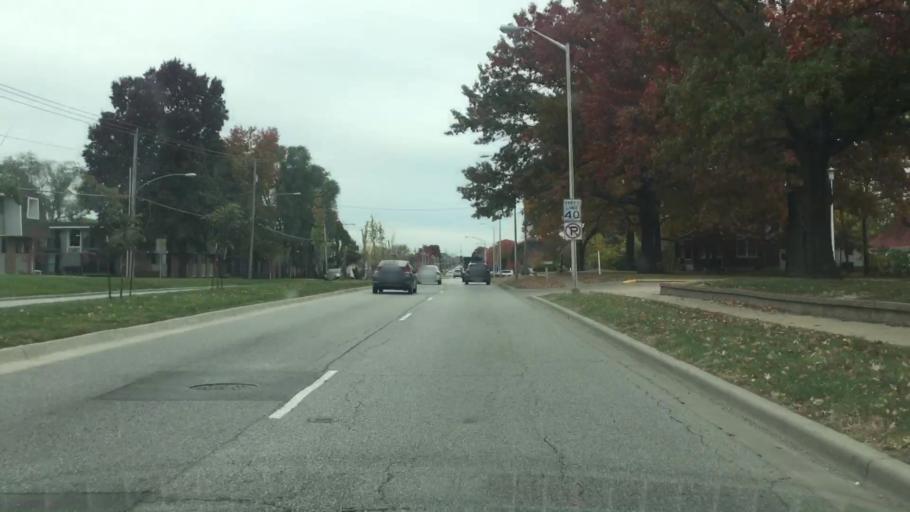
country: US
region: Kansas
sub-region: Johnson County
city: Lenexa
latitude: 38.9921
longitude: -94.7238
